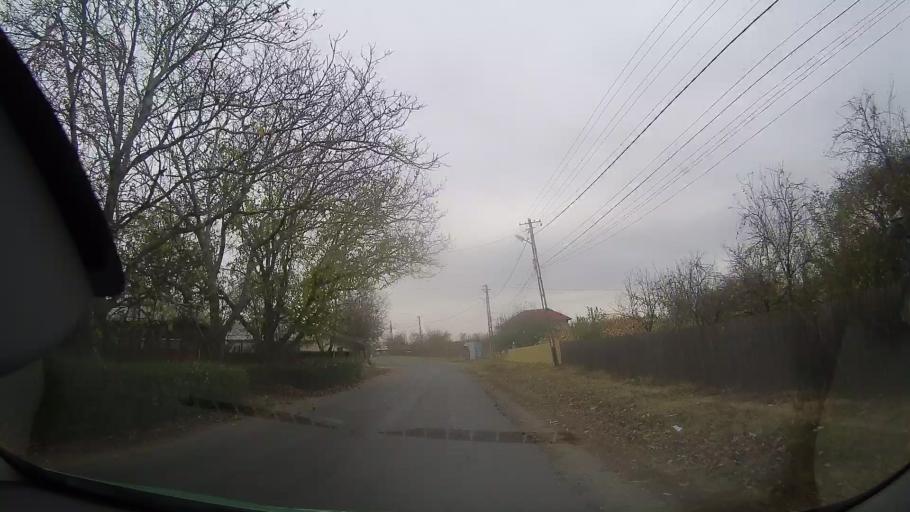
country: RO
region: Buzau
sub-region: Comuna Largu
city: Largu
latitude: 44.9714
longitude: 27.1792
